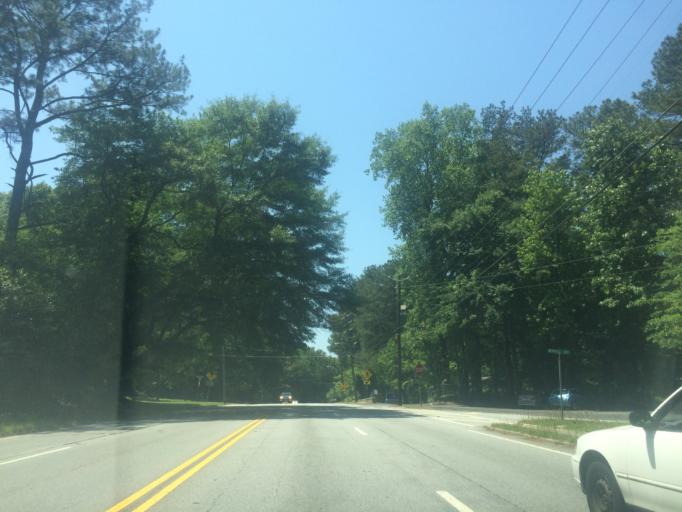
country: US
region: Georgia
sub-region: DeKalb County
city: North Decatur
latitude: 33.7772
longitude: -84.3106
